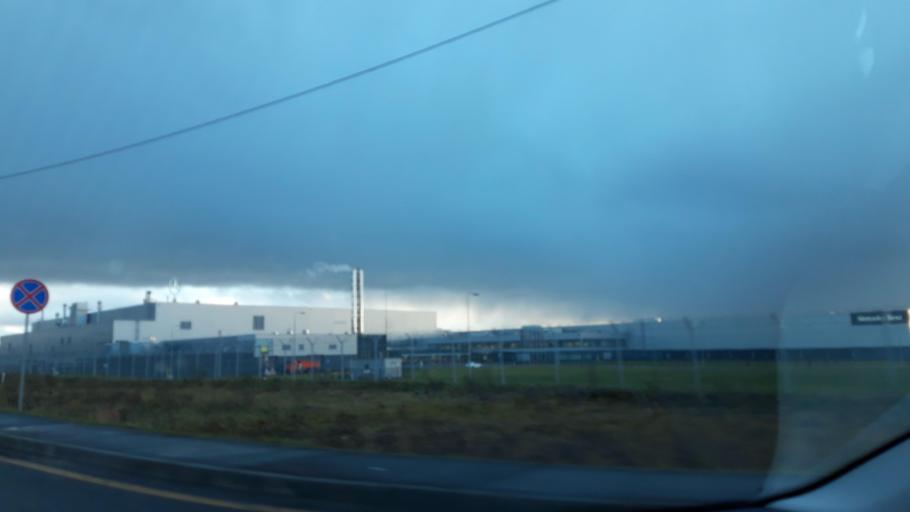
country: RU
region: Moskovskaya
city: Lozhki
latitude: 56.0862
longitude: 37.0823
